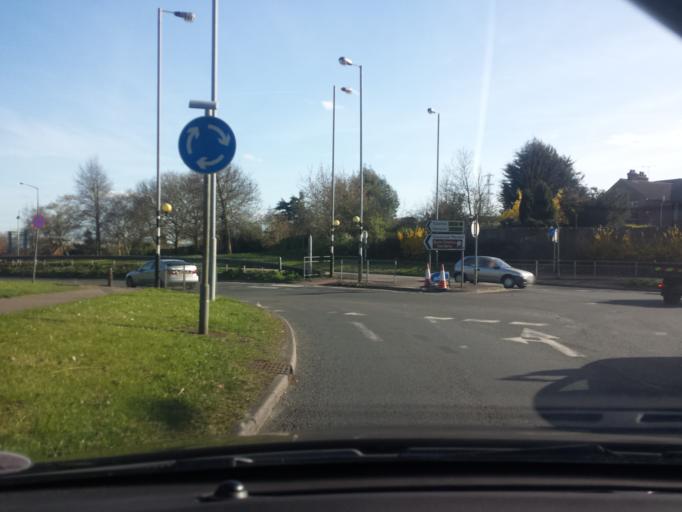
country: GB
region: England
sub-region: Essex
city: Colchester
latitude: 51.8843
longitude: 0.9332
